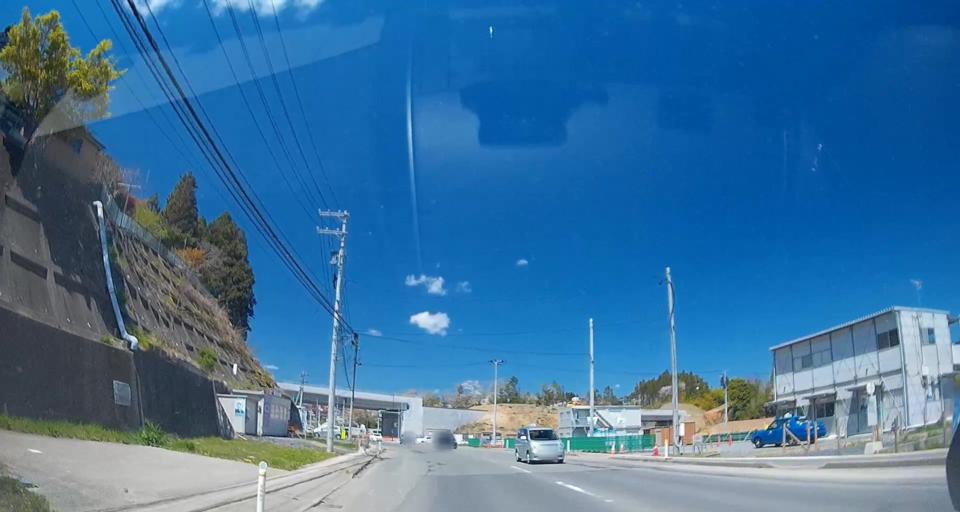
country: JP
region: Iwate
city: Ofunato
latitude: 38.8736
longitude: 141.5830
